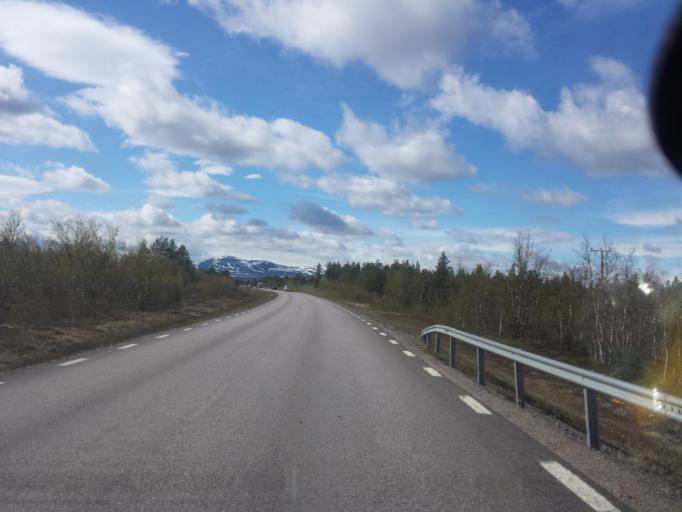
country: SE
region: Norrbotten
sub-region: Kiruna Kommun
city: Kiruna
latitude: 67.9885
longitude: 19.9328
